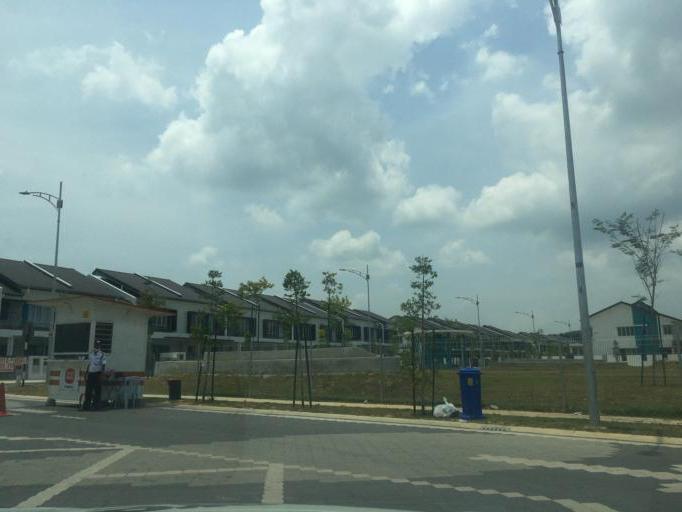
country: MY
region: Putrajaya
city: Putrajaya
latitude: 2.8569
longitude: 101.7036
